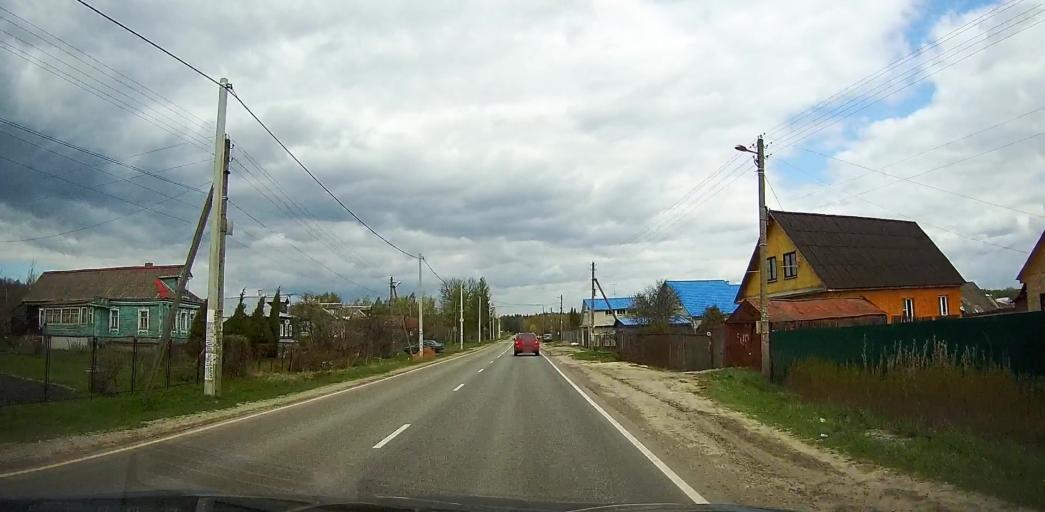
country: RU
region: Moskovskaya
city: Ashitkovo
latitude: 55.4642
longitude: 38.6060
